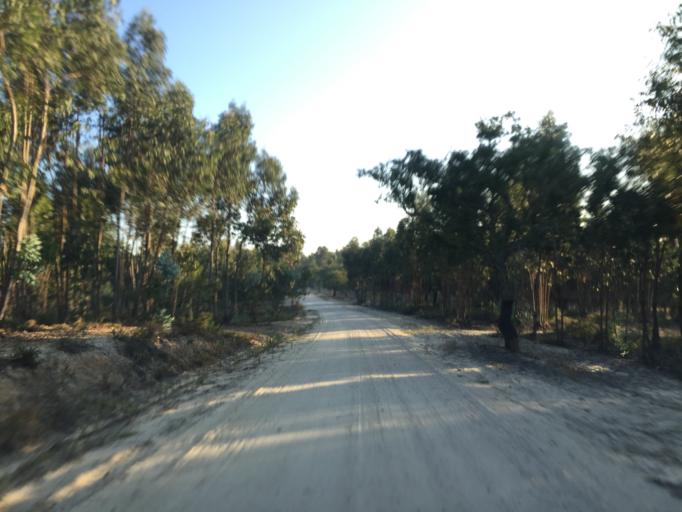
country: PT
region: Portalegre
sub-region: Ponte de Sor
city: Santo Andre
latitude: 39.0771
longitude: -8.3908
